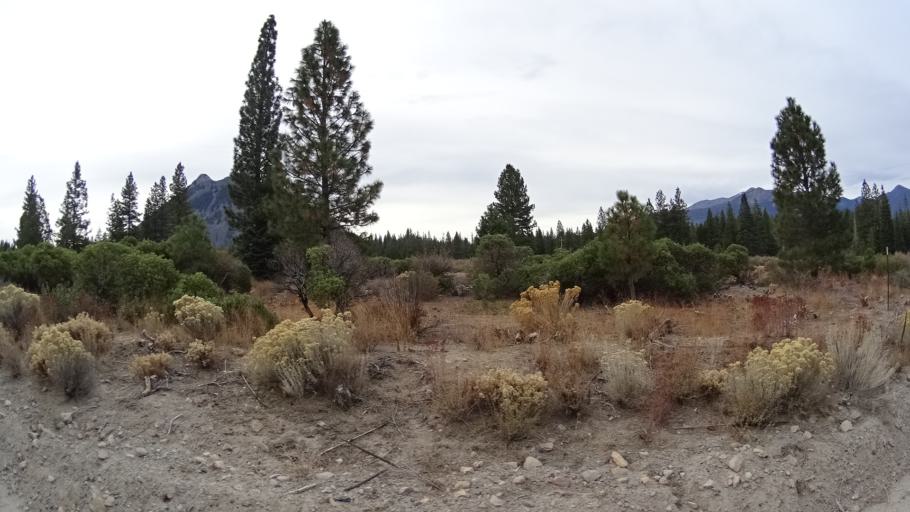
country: US
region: California
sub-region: Siskiyou County
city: Weed
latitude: 41.3927
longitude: -122.3637
